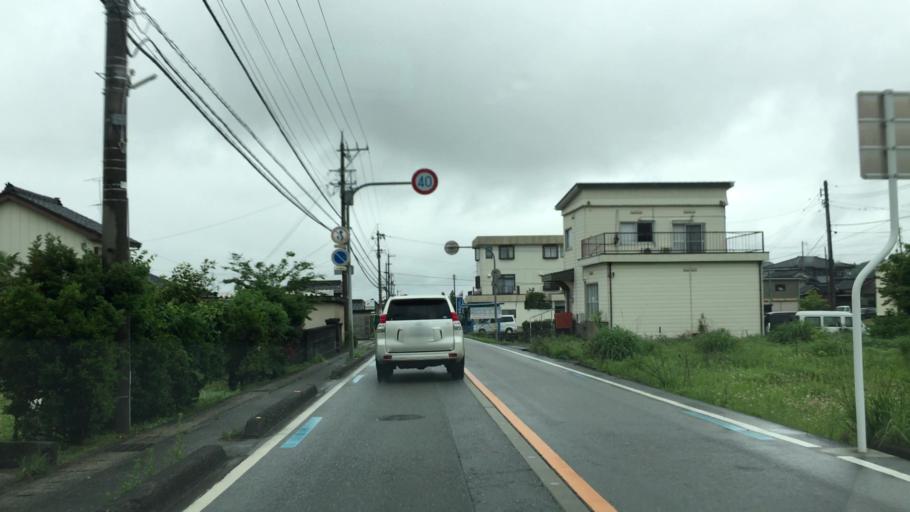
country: JP
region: Toyama
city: Kamiichi
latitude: 36.6073
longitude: 137.3210
